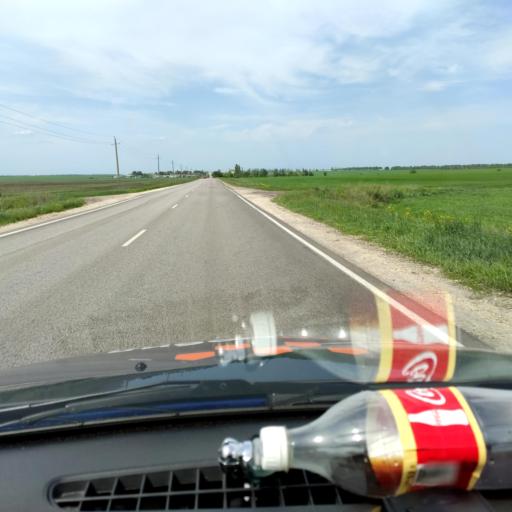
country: RU
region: Voronezj
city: Novaya Usman'
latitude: 51.5642
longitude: 39.3759
